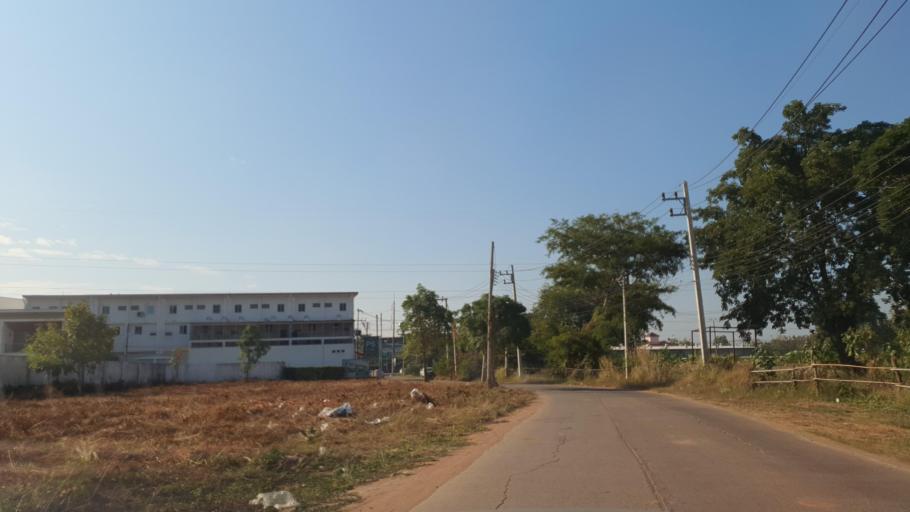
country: TH
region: Khon Kaen
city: Khon Kaen
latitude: 16.4135
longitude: 102.8117
